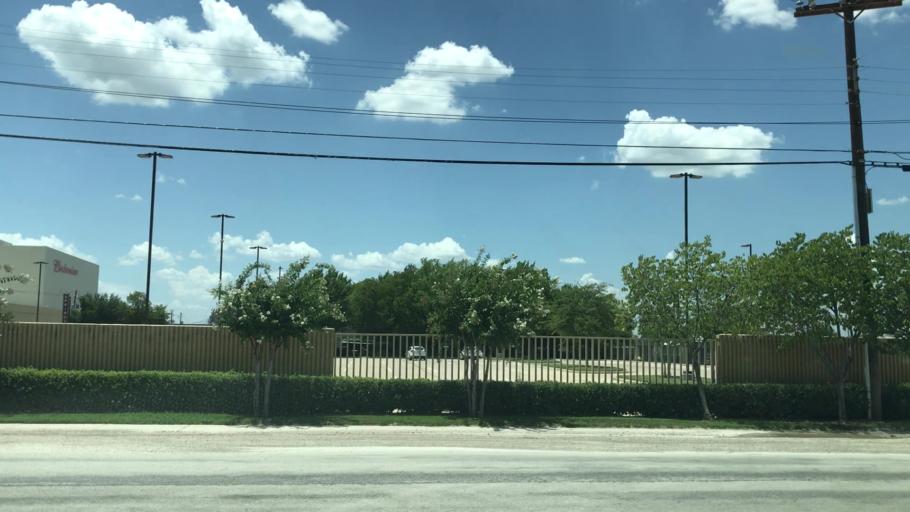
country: US
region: Texas
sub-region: Dallas County
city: Dallas
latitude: 32.8198
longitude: -96.8513
